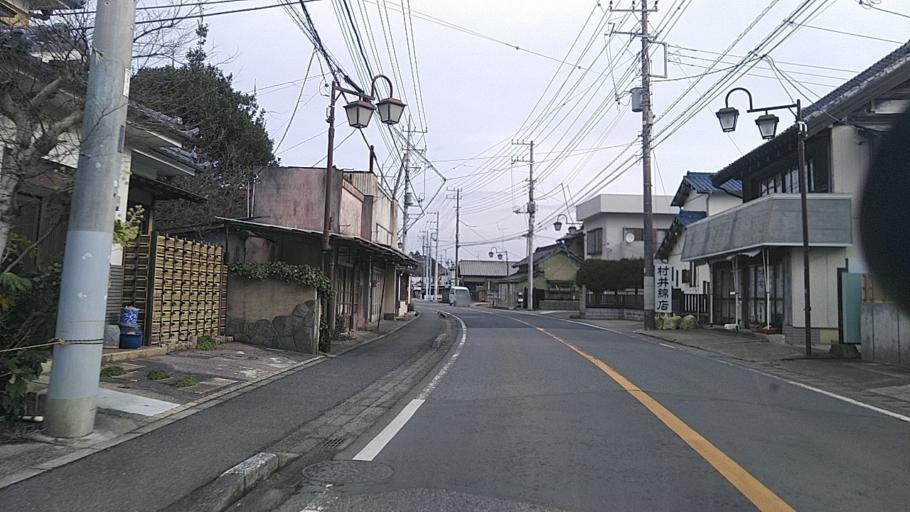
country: JP
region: Chiba
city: Togane
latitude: 35.5664
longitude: 140.3668
